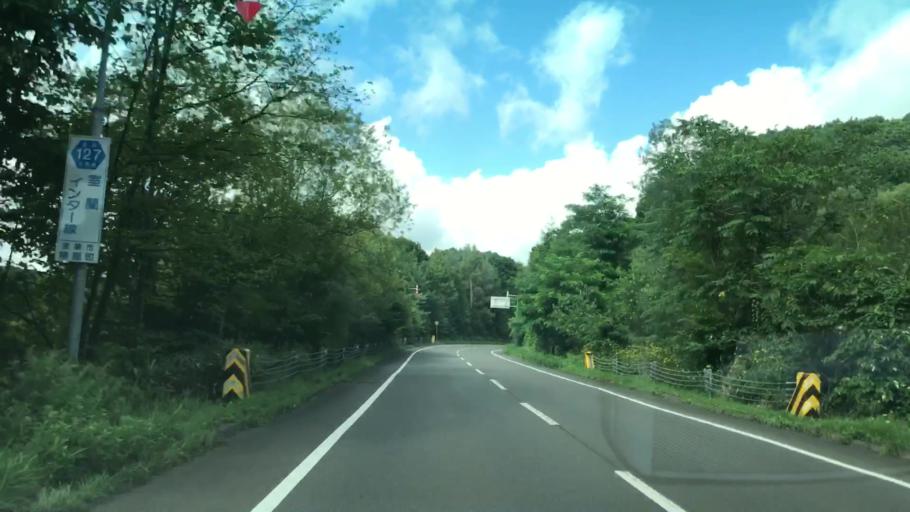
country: JP
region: Hokkaido
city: Muroran
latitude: 42.3702
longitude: 140.9581
